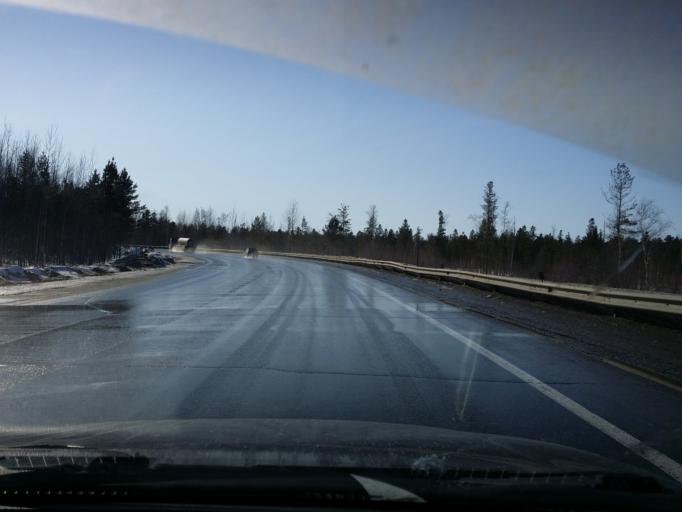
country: RU
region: Khanty-Mansiyskiy Avtonomnyy Okrug
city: Langepas
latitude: 61.1818
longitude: 75.5146
